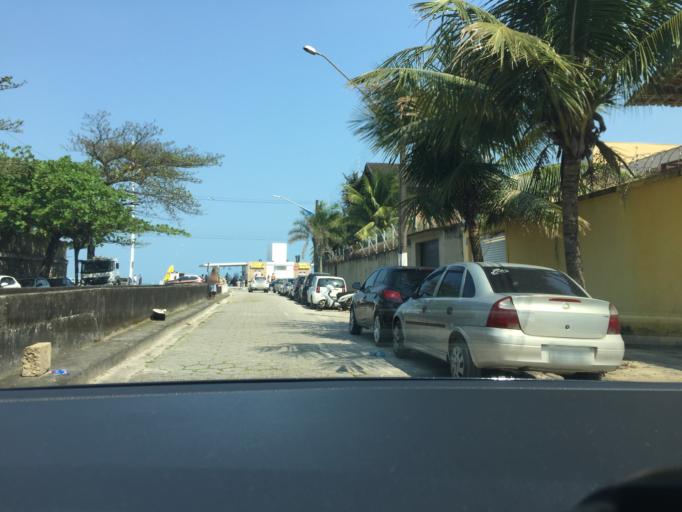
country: BR
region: Sao Paulo
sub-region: Guaruja
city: Guaruja
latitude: -23.9848
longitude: -46.2209
